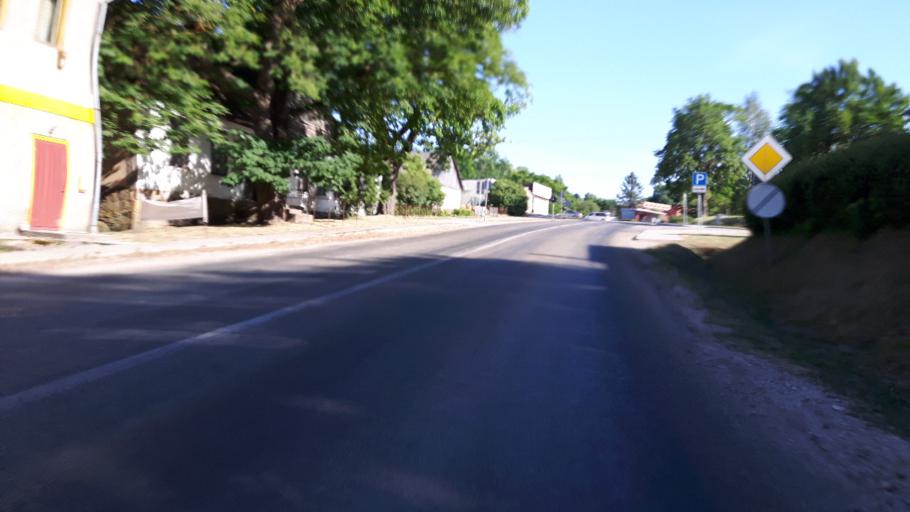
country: LV
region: Talsu Rajons
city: Stende
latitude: 57.0696
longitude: 22.2931
